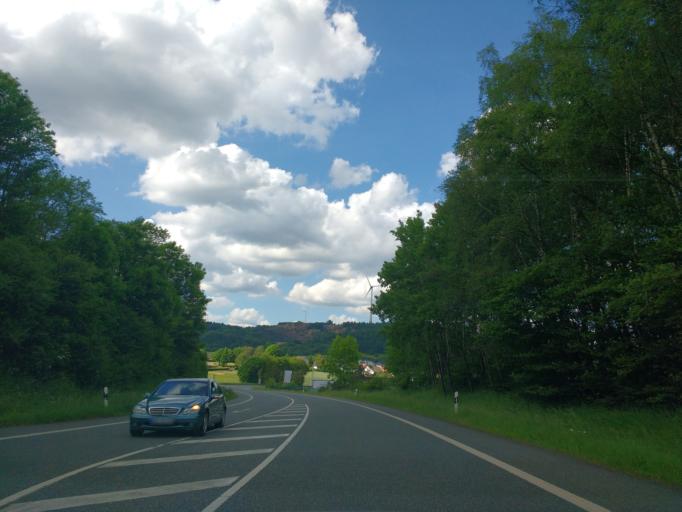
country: DE
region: Hesse
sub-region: Regierungsbezirk Giessen
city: Breidenbach
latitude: 50.8507
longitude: 8.4110
